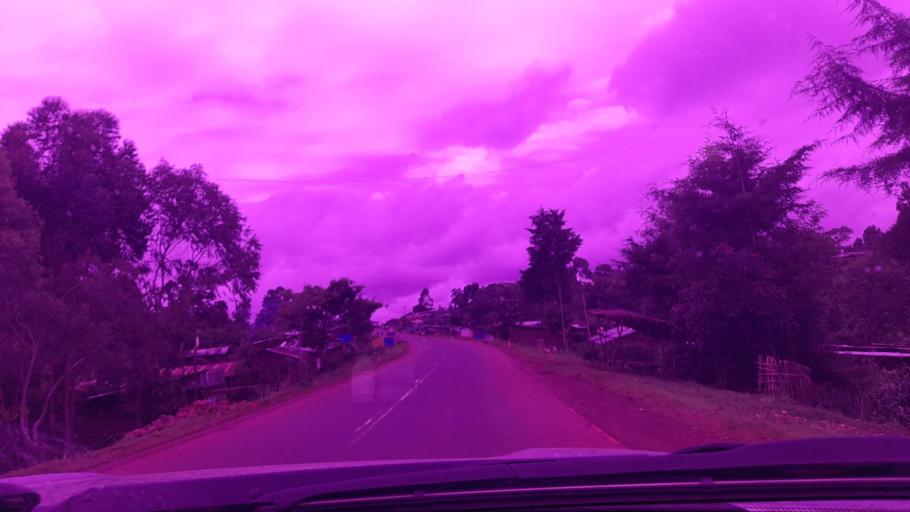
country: ET
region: Southern Nations, Nationalities, and People's Region
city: Bonga
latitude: 7.2991
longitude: 35.9899
